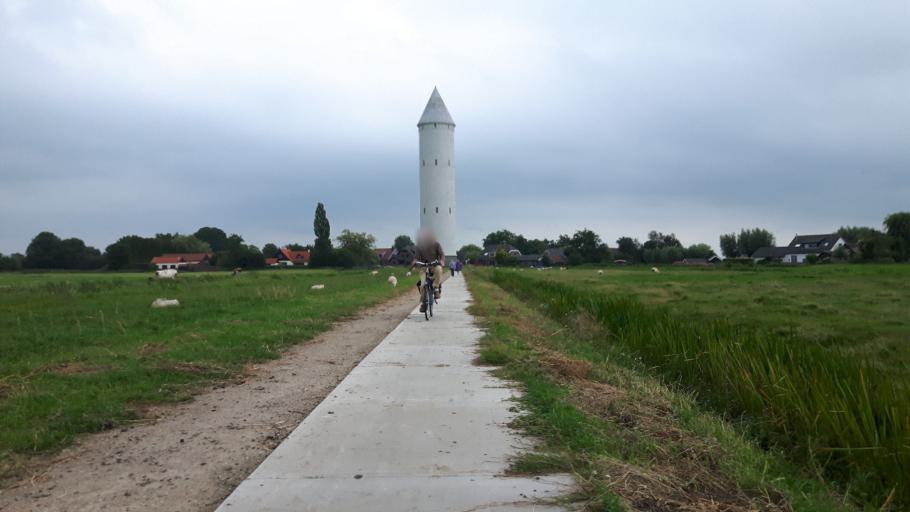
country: NL
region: South Holland
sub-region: Gemeente Nieuwkoop
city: Nieuwkoop
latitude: 52.1218
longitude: 4.7858
